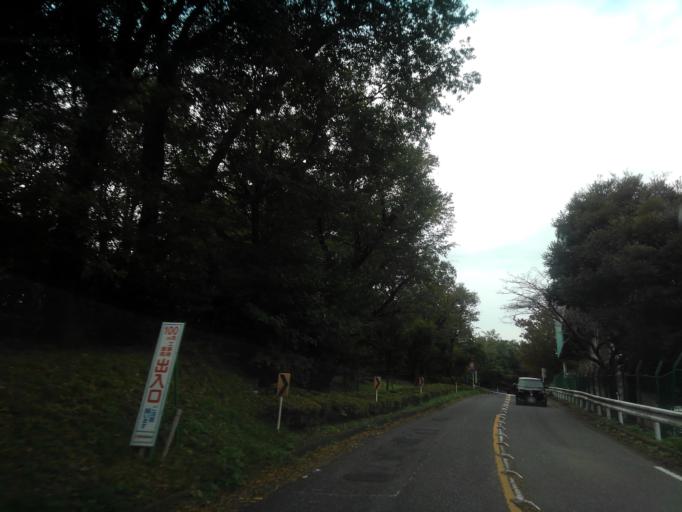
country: JP
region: Tokyo
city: Higashimurayama-shi
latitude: 35.7662
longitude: 139.4197
